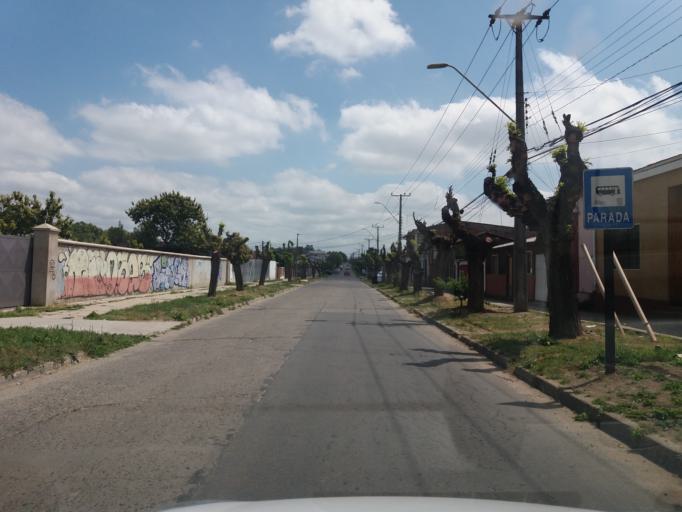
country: CL
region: Valparaiso
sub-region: Provincia de Marga Marga
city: Limache
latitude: -32.9874
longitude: -71.2673
